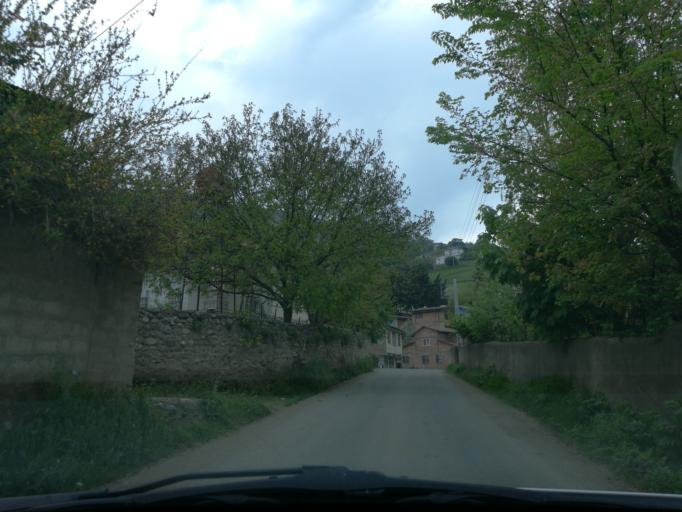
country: IR
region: Mazandaran
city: Chalus
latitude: 36.5316
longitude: 51.2291
